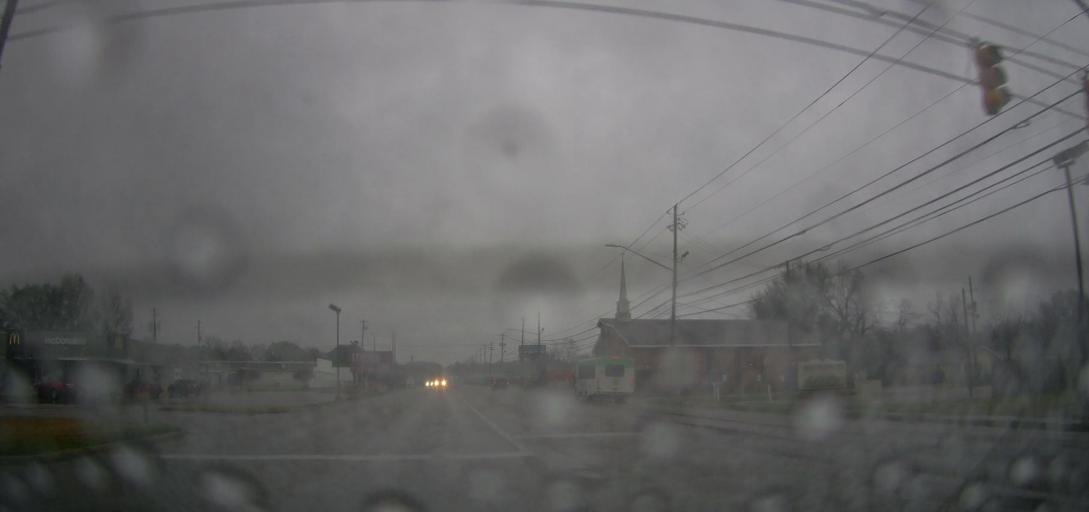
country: US
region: Alabama
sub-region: Montgomery County
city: Montgomery
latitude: 32.3692
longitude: -86.3458
